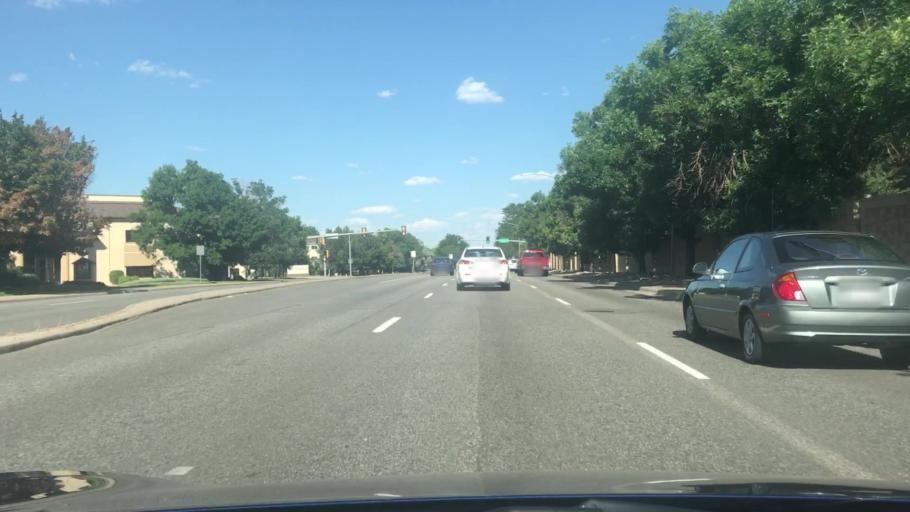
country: US
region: Colorado
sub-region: Arapahoe County
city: Dove Valley
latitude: 39.6530
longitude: -104.8215
